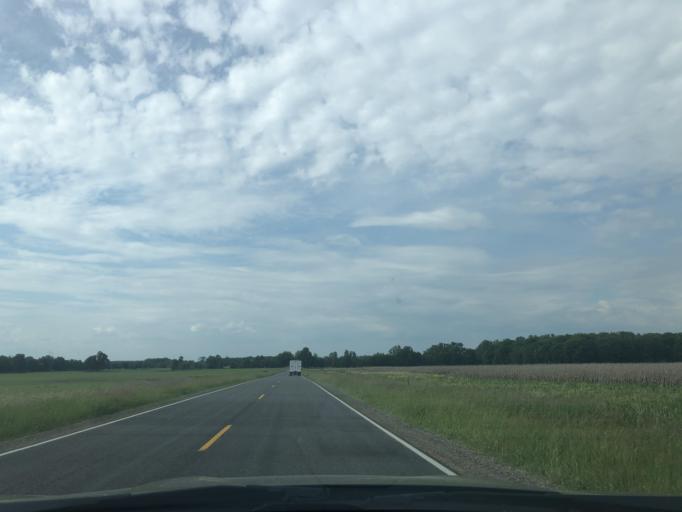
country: US
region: Michigan
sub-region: Clinton County
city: Saint Johns
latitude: 42.9593
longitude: -84.4837
